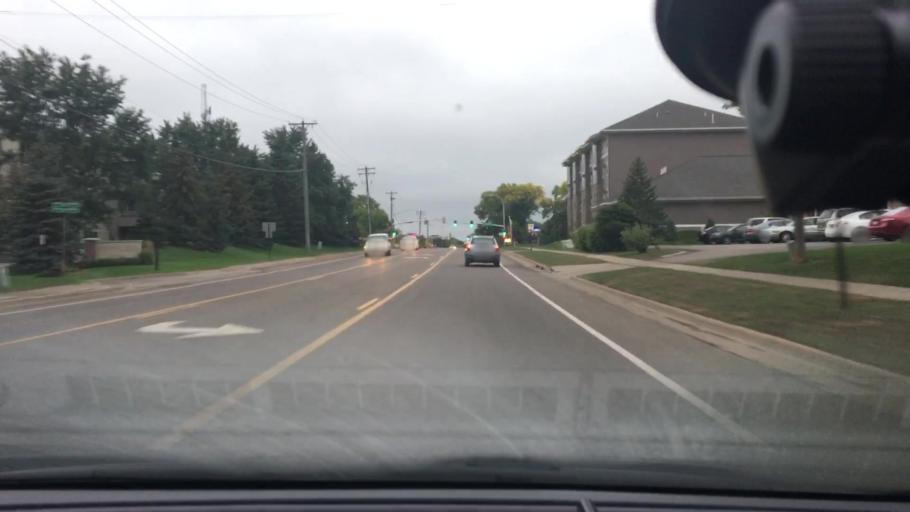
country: US
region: Minnesota
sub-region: Hennepin County
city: New Hope
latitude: 45.0075
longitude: -93.3958
